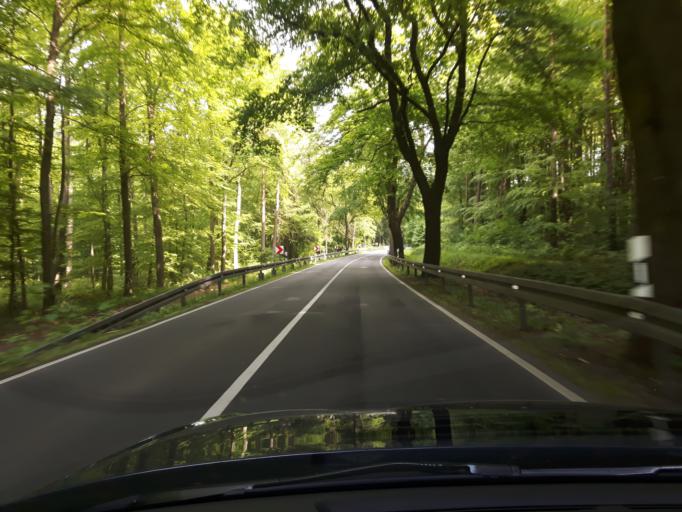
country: DE
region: Mecklenburg-Vorpommern
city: Gross Wokern
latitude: 53.6263
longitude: 12.4684
